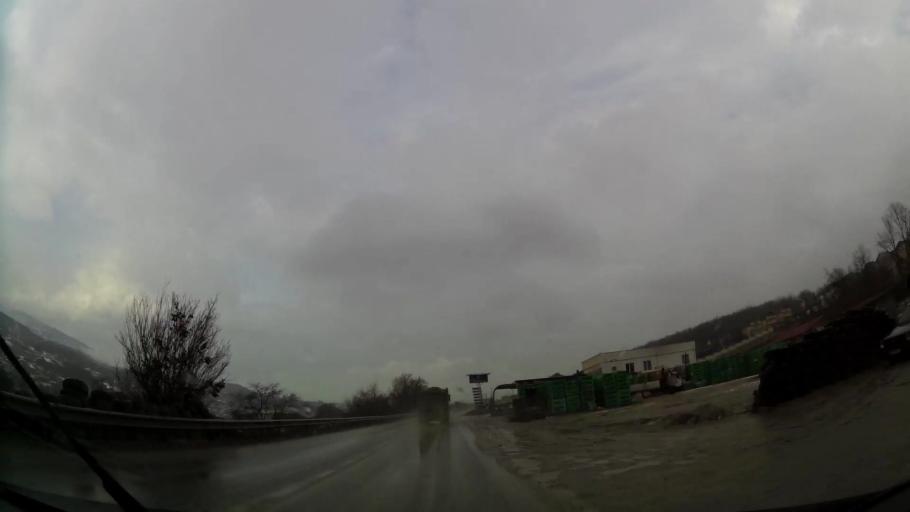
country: XK
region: Ferizaj
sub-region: Komuna e Kacanikut
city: Kacanik
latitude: 42.2395
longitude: 21.2447
